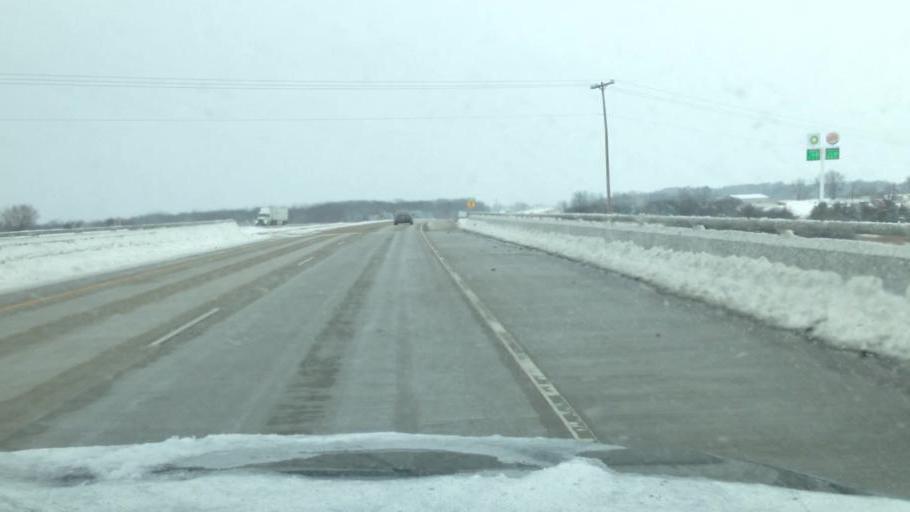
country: US
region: Wisconsin
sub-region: Walworth County
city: Elkhorn
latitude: 42.6917
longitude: -88.5037
